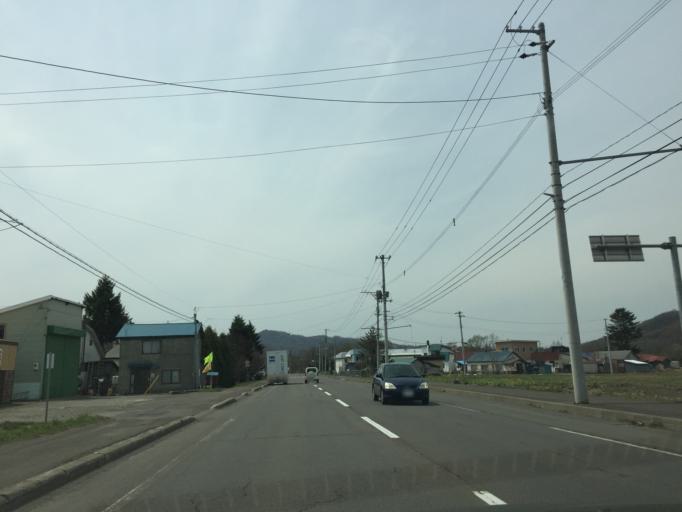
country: JP
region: Hokkaido
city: Akabira
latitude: 43.5412
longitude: 142.1119
